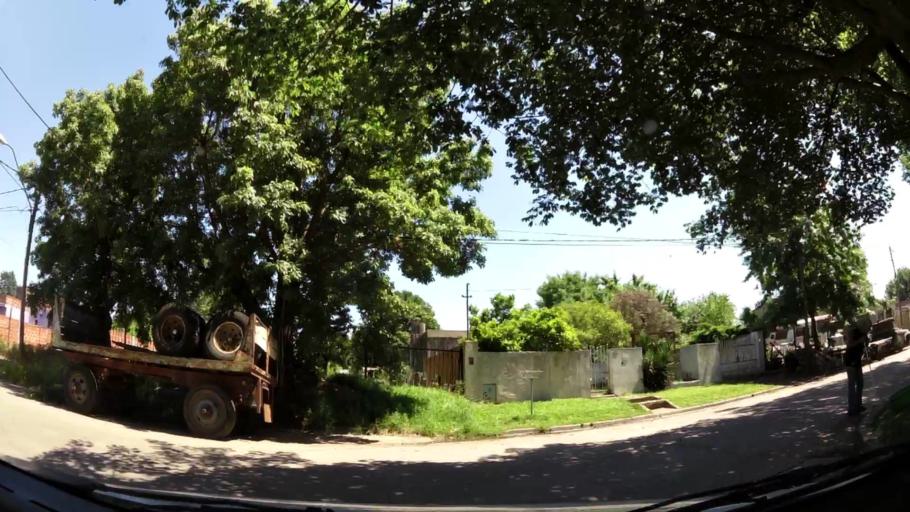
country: AR
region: Buenos Aires
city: Ituzaingo
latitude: -34.6607
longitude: -58.6862
